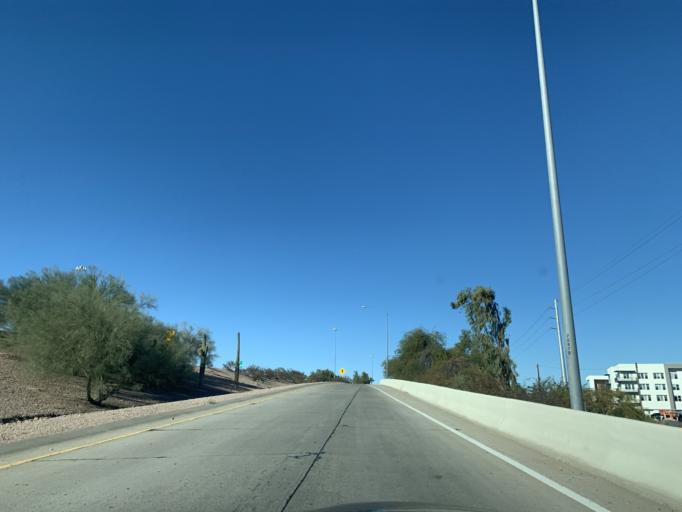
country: US
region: Arizona
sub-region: Maricopa County
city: Tempe Junction
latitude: 33.4486
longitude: -111.9814
